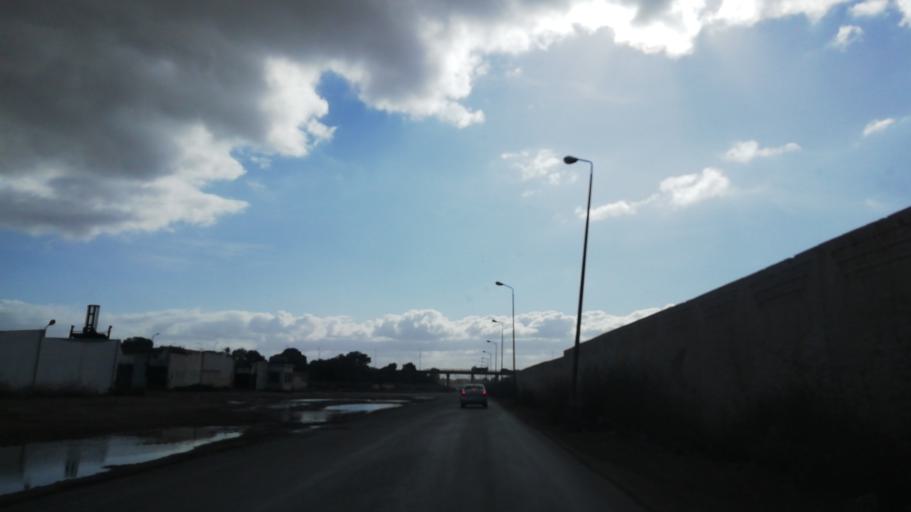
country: DZ
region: Oran
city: Es Senia
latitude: 35.6260
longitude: -0.5907
